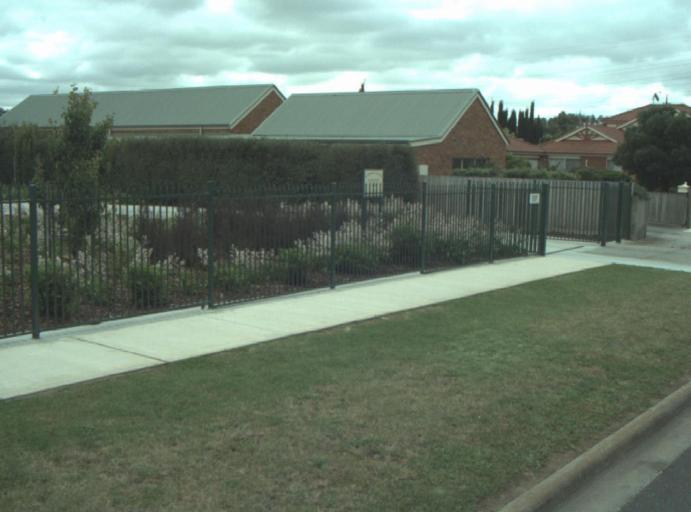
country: AU
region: Victoria
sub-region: Greater Geelong
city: Bell Post Hill
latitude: -38.0716
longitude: 144.3376
